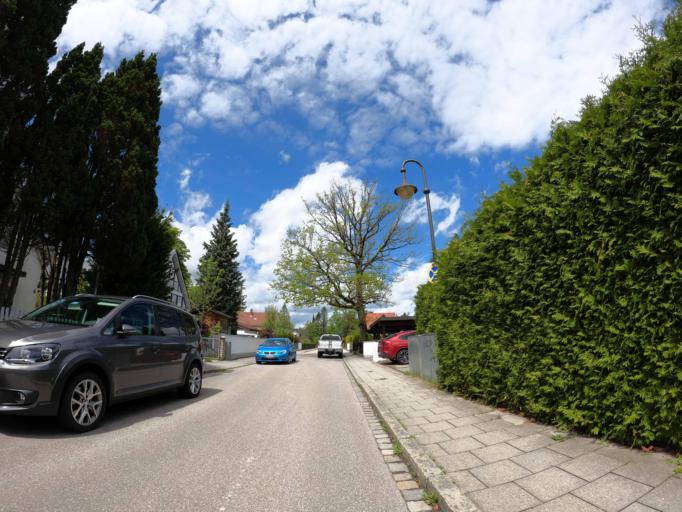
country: DE
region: Bavaria
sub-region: Upper Bavaria
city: Ottobrunn
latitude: 48.0664
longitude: 11.6756
